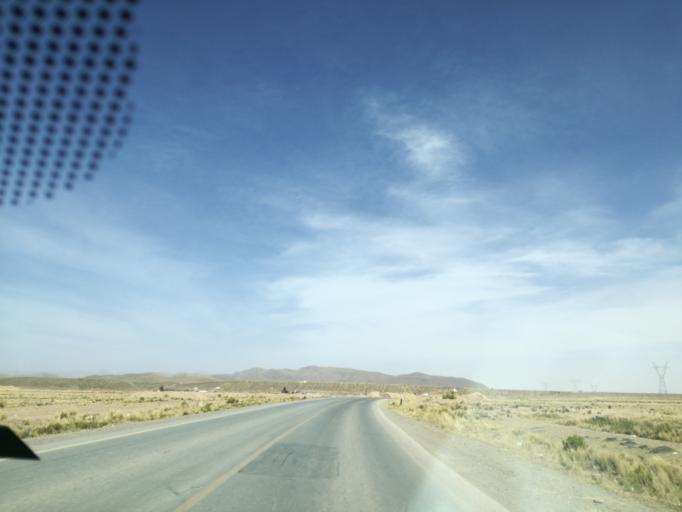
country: BO
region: Oruro
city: Oruro
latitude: -17.8118
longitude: -67.0207
